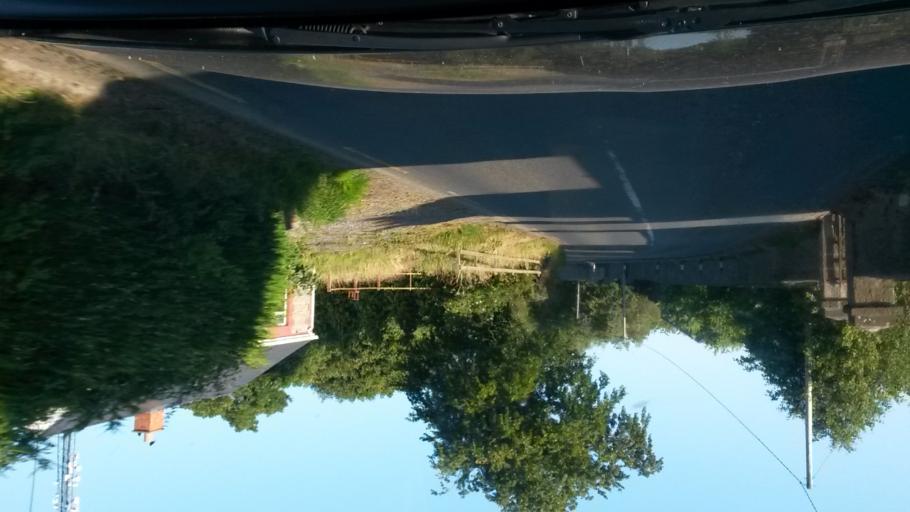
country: IE
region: Leinster
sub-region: Fingal County
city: Blanchardstown
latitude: 53.4420
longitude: -6.3491
